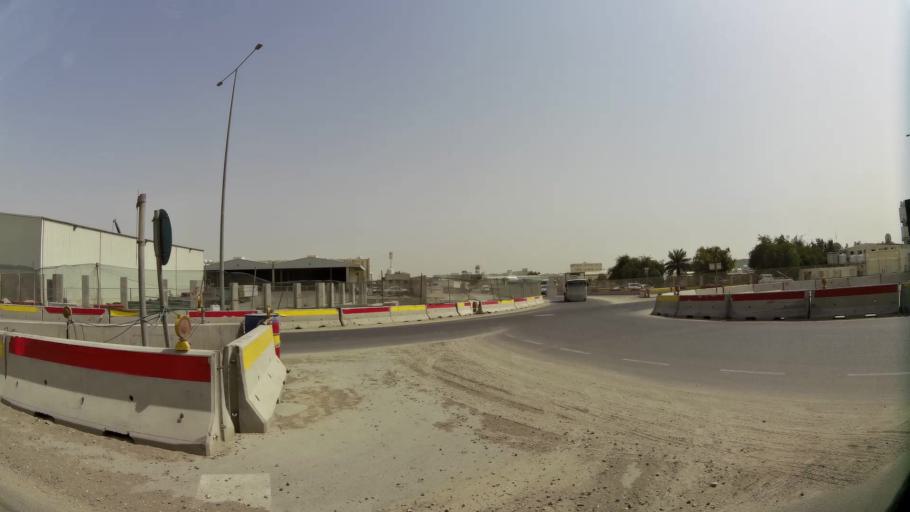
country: QA
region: Baladiyat ar Rayyan
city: Ar Rayyan
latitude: 25.1879
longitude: 51.4216
